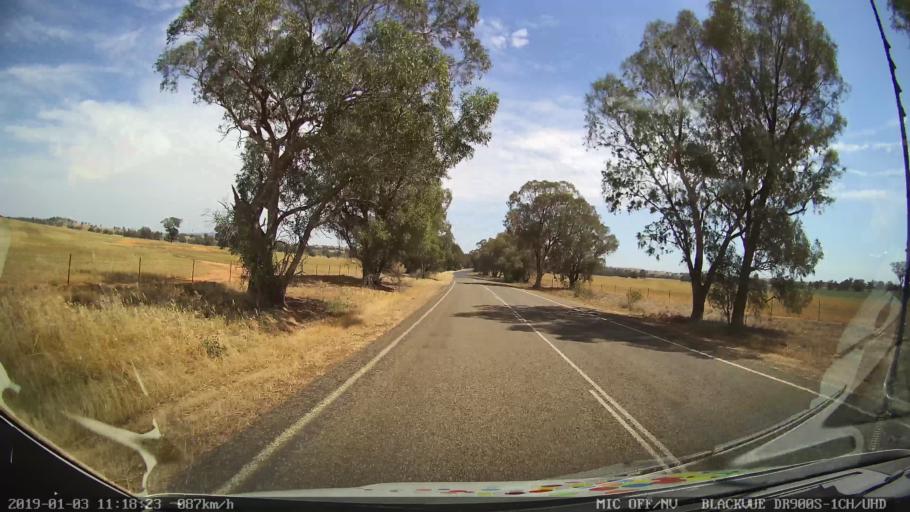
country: AU
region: New South Wales
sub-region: Young
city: Young
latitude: -34.1267
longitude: 148.2628
